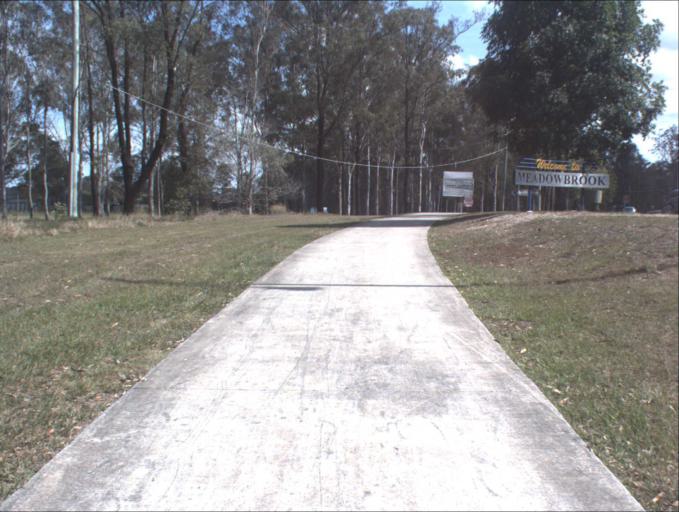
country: AU
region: Queensland
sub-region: Logan
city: Slacks Creek
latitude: -27.6543
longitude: 153.1458
